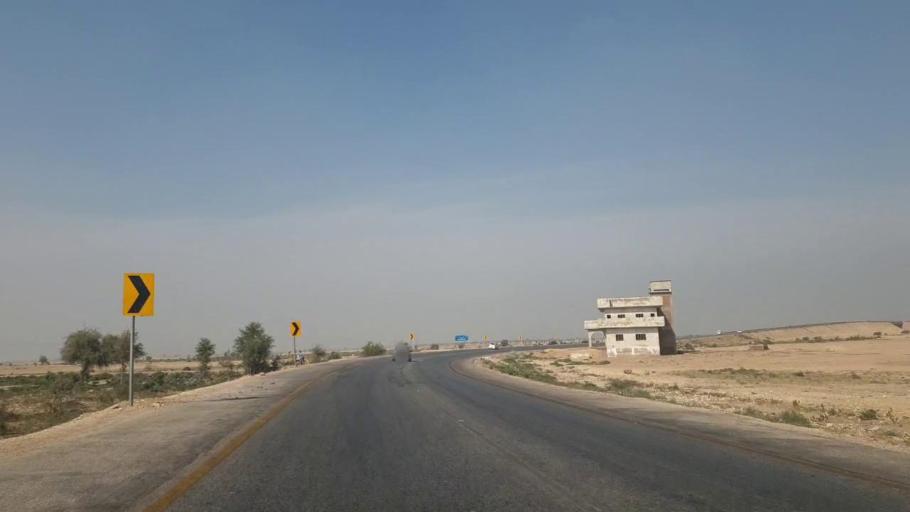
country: PK
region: Sindh
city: Hala
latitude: 25.8544
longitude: 68.2574
